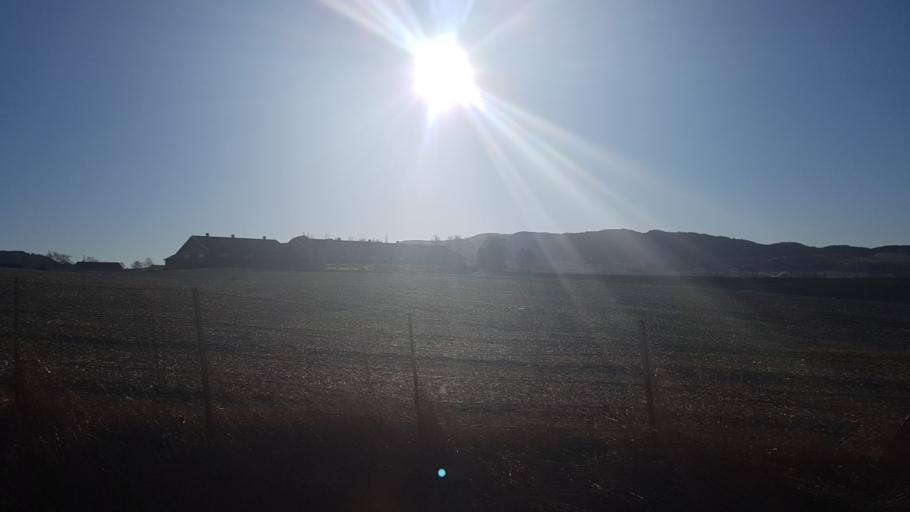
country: NO
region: Nord-Trondelag
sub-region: Levanger
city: Skogn
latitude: 63.6982
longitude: 11.1841
